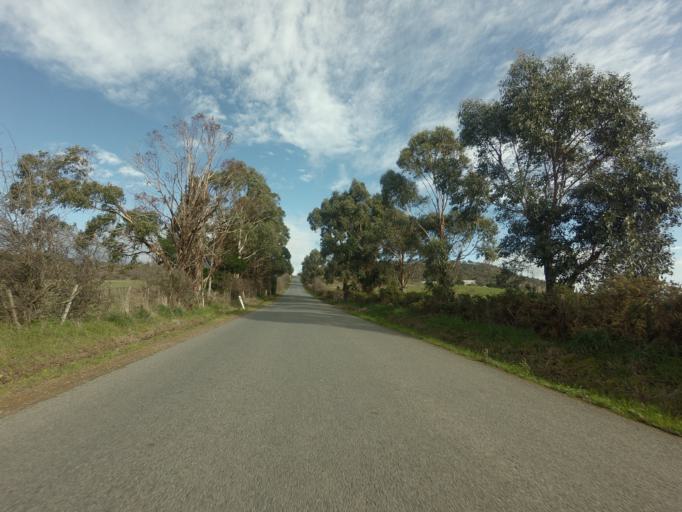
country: AU
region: Tasmania
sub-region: Derwent Valley
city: New Norfolk
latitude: -42.7743
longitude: 147.0236
